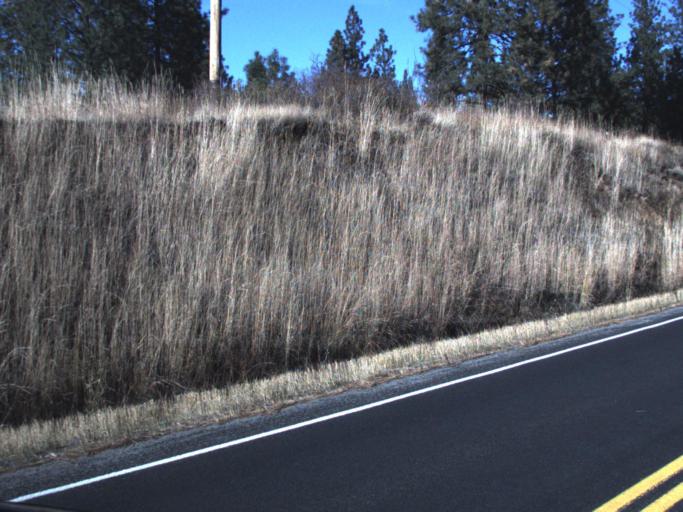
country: US
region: Washington
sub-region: Lincoln County
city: Davenport
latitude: 47.9600
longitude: -118.3079
